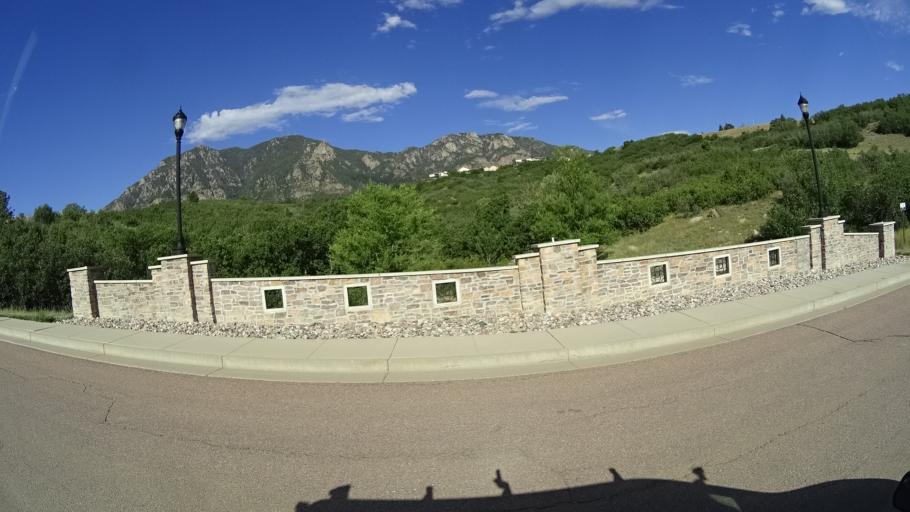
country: US
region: Colorado
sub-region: El Paso County
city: Fort Carson
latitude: 38.7552
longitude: -104.8207
